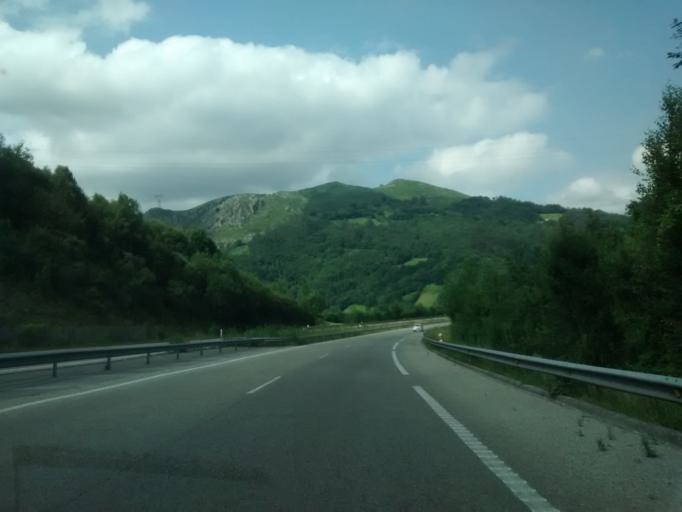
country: ES
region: Asturias
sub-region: Province of Asturias
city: Sama
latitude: 43.3184
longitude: -5.7449
